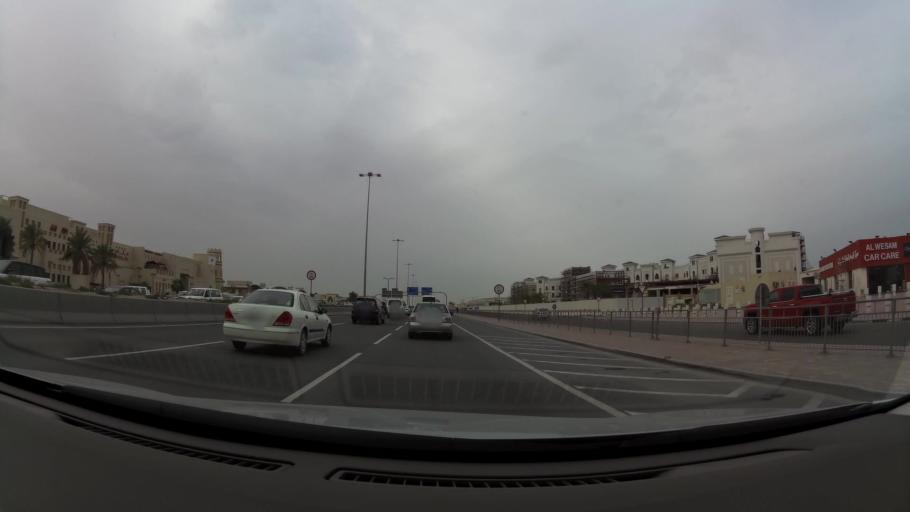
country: QA
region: Baladiyat ar Rayyan
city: Ar Rayyan
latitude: 25.3360
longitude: 51.4625
